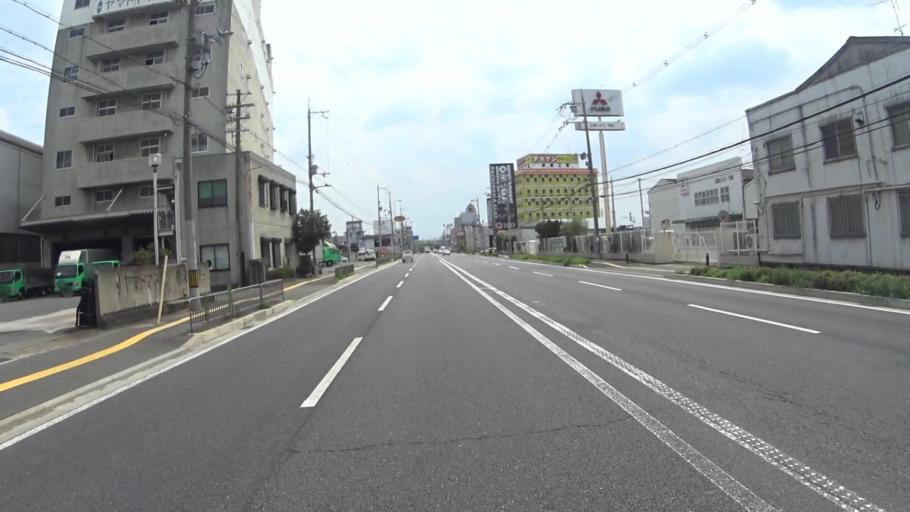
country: JP
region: Kyoto
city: Muko
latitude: 34.9420
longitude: 135.7167
